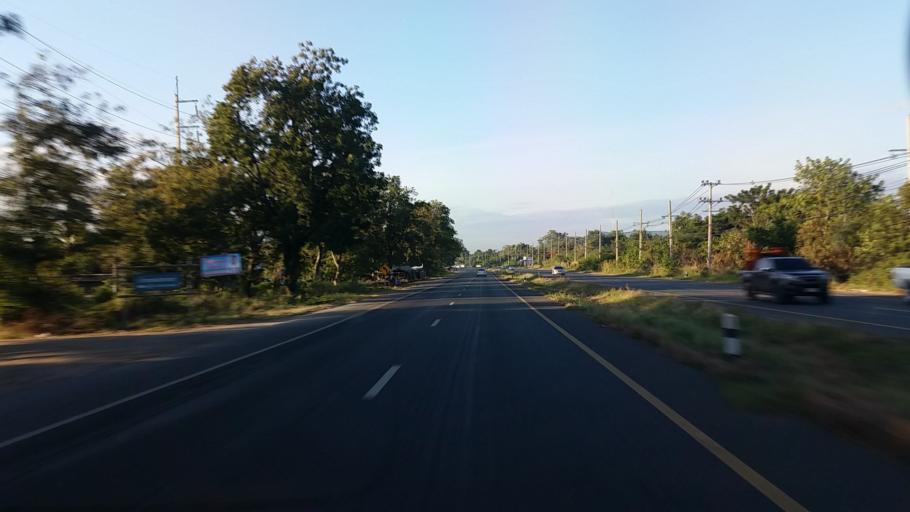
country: TH
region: Lop Buri
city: Chai Badan
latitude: 15.1825
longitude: 101.0733
